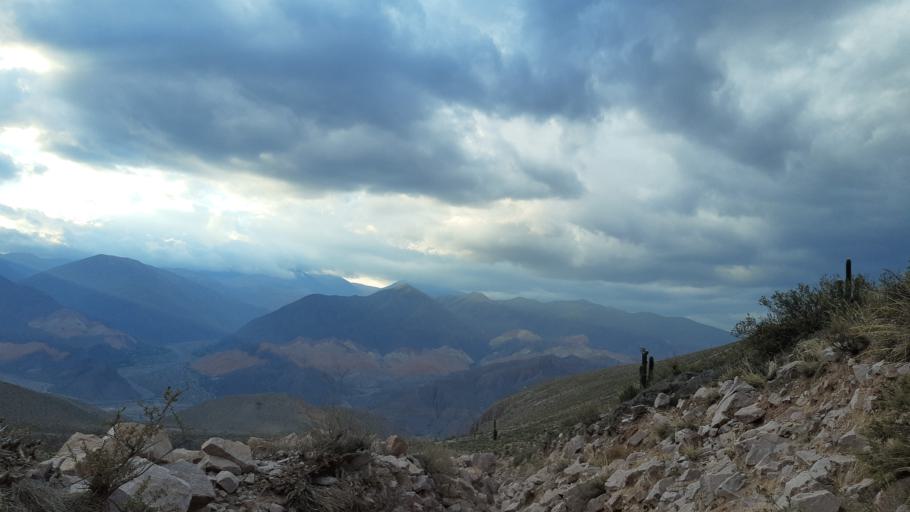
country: AR
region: Jujuy
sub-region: Departamento de Tilcara
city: Tilcara
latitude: -23.5923
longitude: -65.3823
